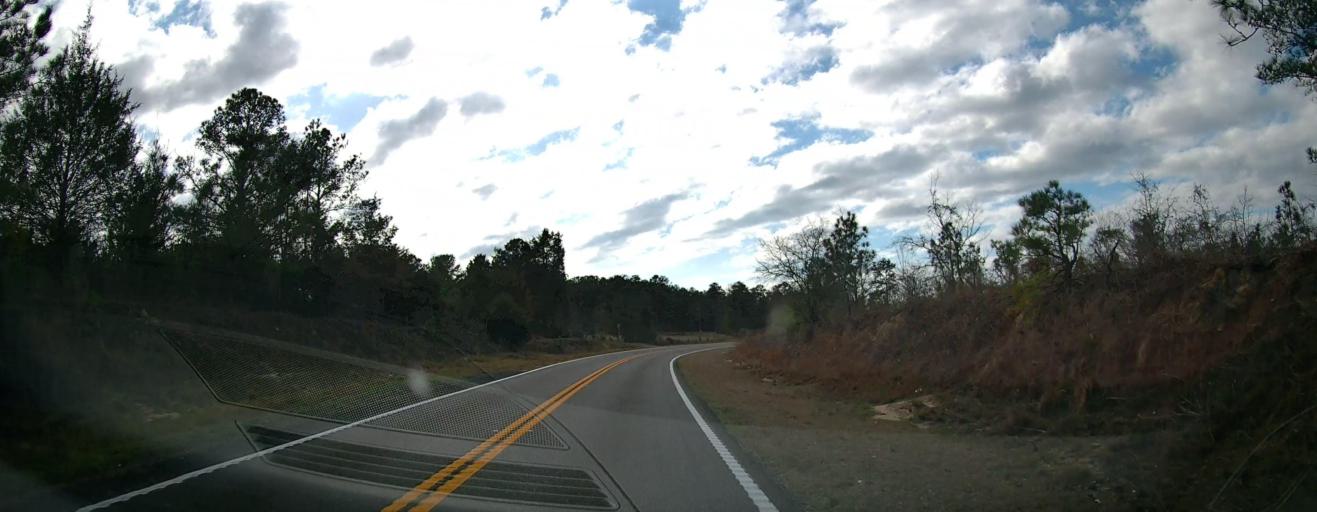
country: US
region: Georgia
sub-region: Marion County
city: Buena Vista
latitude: 32.4378
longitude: -84.5045
